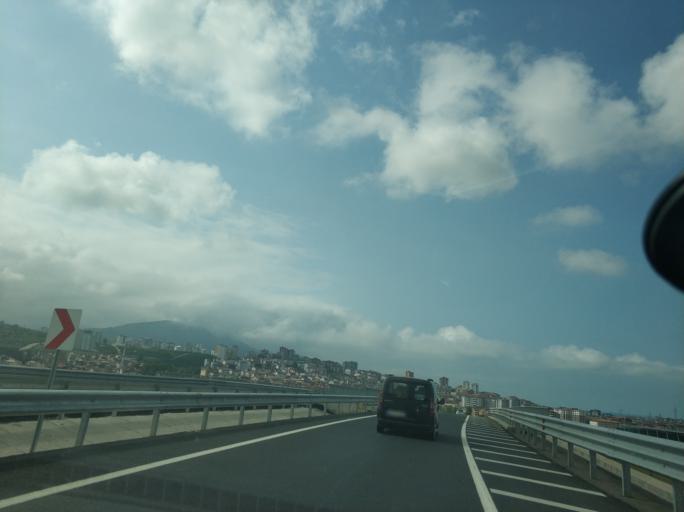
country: TR
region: Ordu
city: Ordu
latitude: 40.9532
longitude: 37.9030
